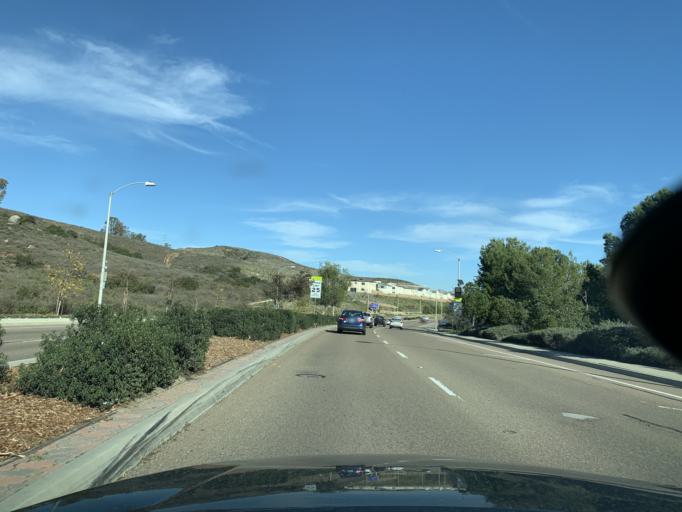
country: US
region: California
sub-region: San Diego County
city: Santee
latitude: 32.8479
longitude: -117.0211
